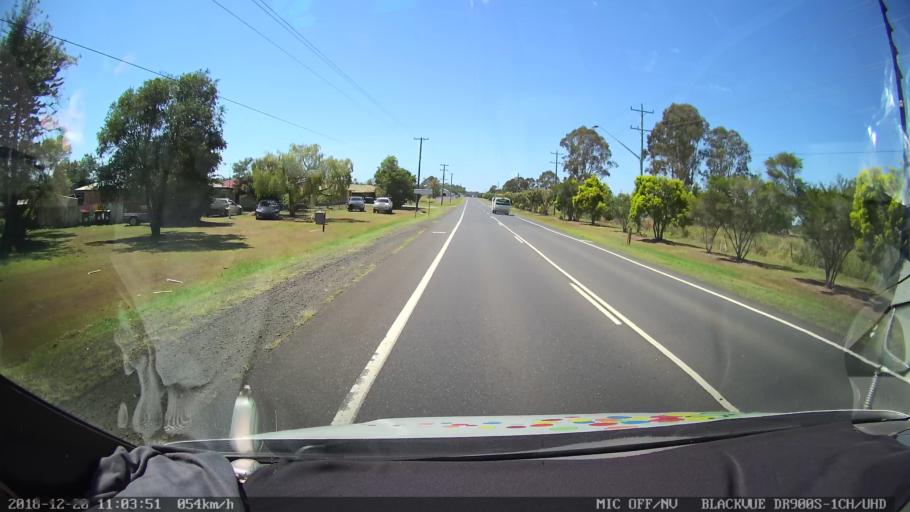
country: AU
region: New South Wales
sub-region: Richmond Valley
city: Casino
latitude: -28.8800
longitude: 153.0427
